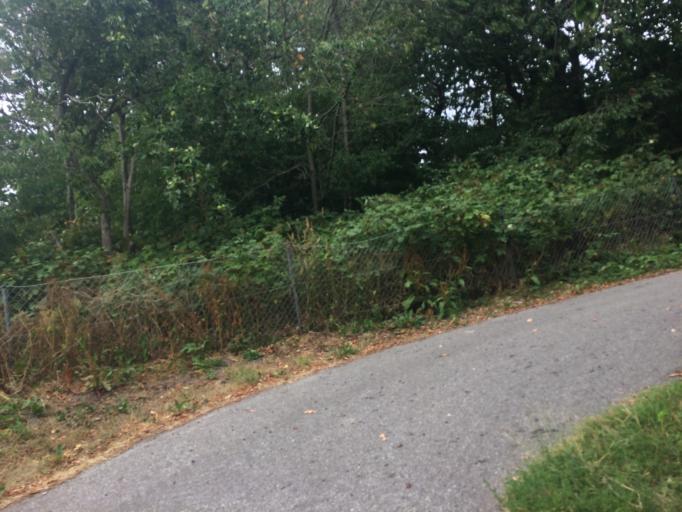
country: DK
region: Central Jutland
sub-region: Struer Kommune
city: Struer
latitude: 56.4815
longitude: 8.6098
